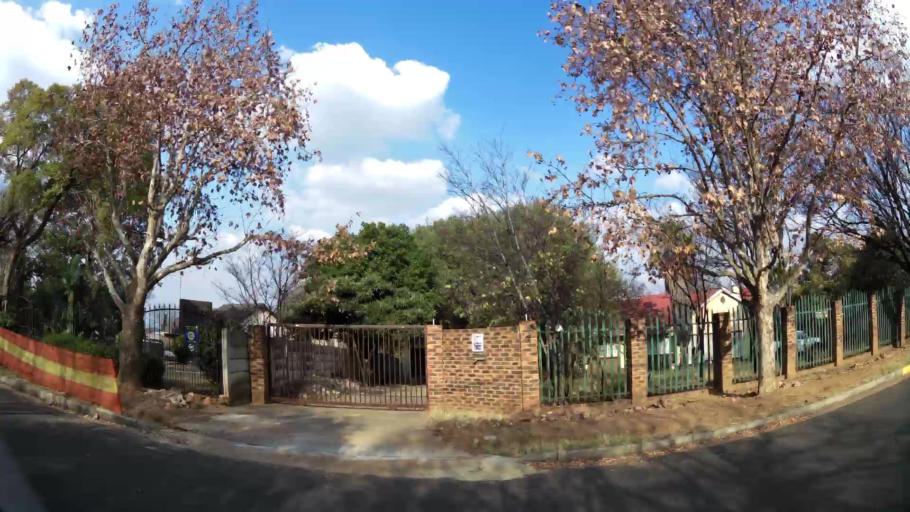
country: ZA
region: Gauteng
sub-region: Ekurhuleni Metropolitan Municipality
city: Germiston
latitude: -26.2439
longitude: 28.1852
